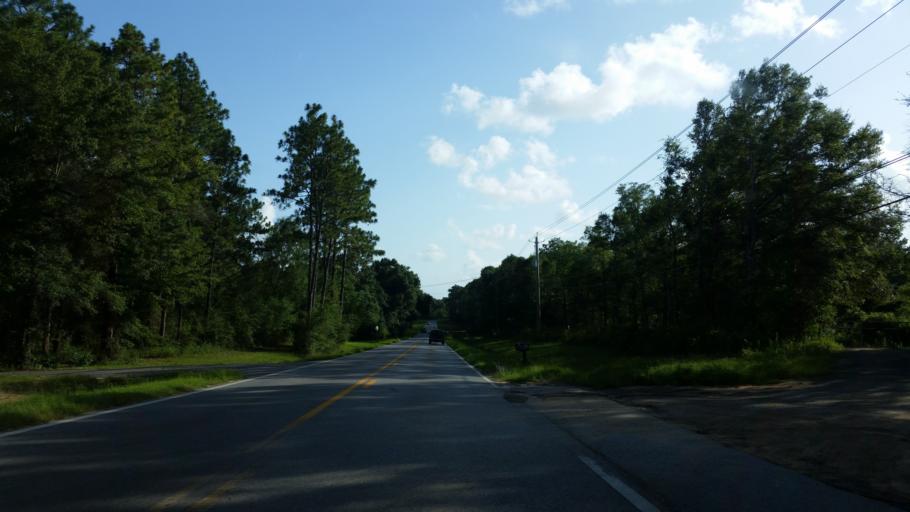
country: US
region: Florida
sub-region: Santa Rosa County
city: Pace
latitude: 30.5654
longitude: -87.1049
